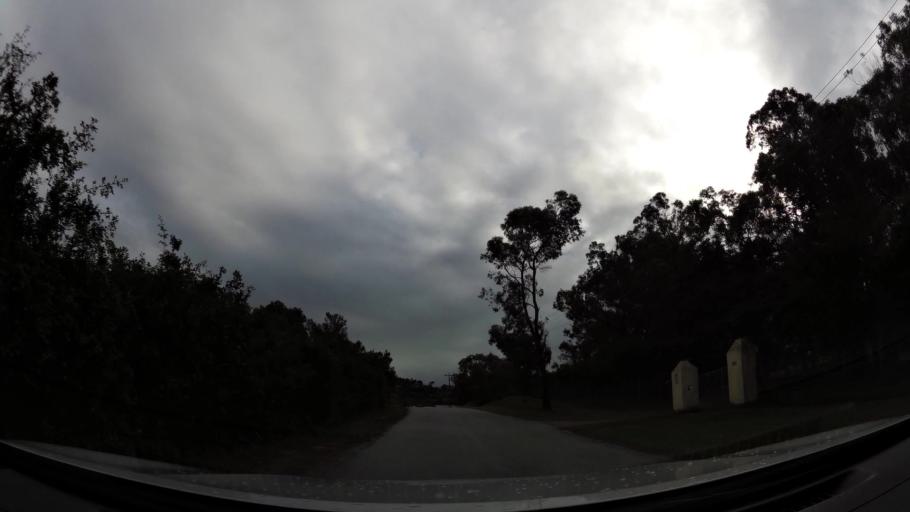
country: ZA
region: Eastern Cape
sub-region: Nelson Mandela Bay Metropolitan Municipality
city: Port Elizabeth
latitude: -34.0142
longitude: 25.4974
